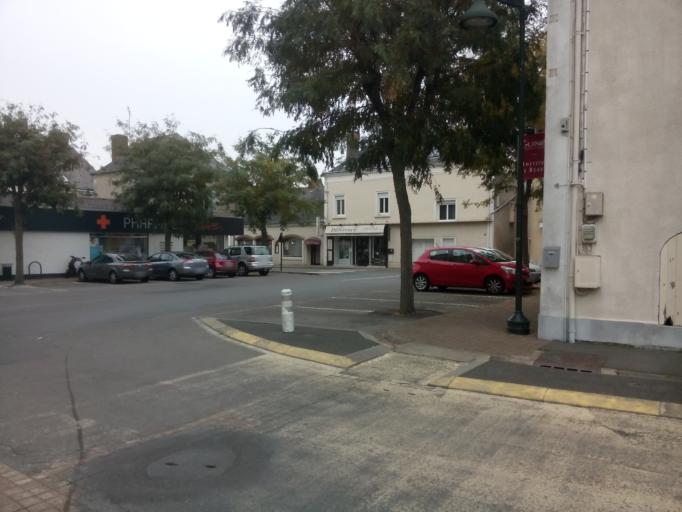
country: FR
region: Pays de la Loire
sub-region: Departement de Maine-et-Loire
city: Tierce
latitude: 47.6152
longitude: -0.4689
